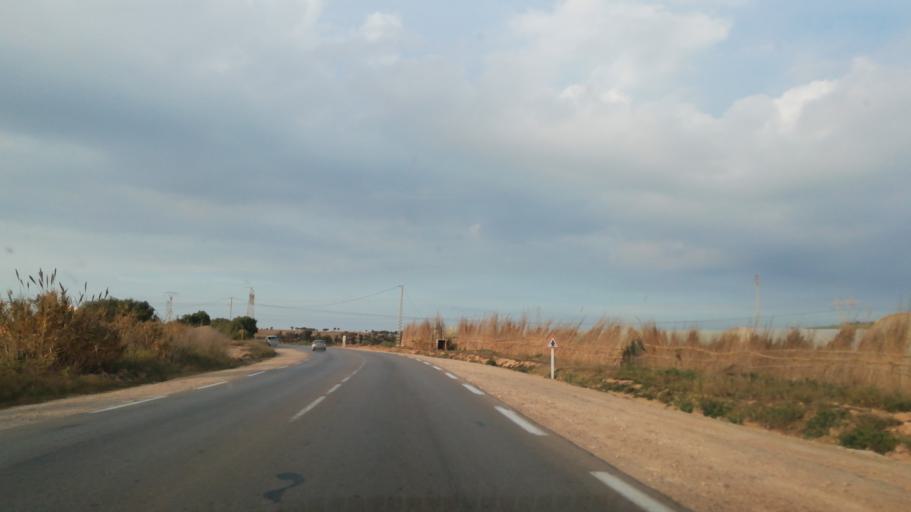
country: DZ
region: Oran
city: Ain el Bya
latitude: 35.7787
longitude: -0.0973
